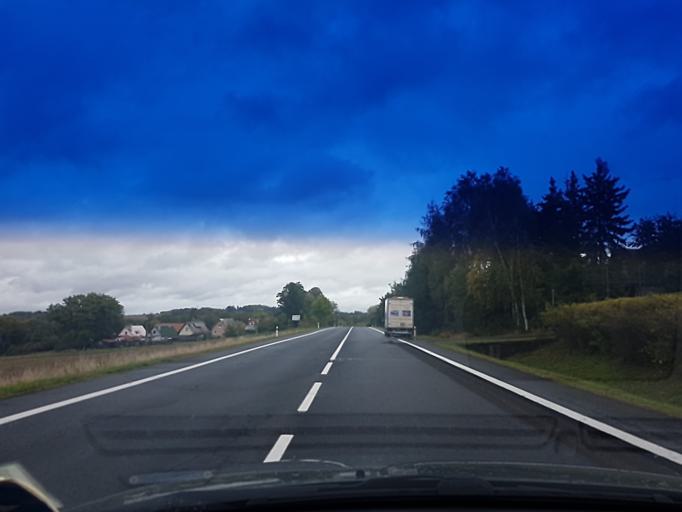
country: CZ
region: Karlovarsky
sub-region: Okres Cheb
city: Frantiskovy Lazne
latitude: 50.0815
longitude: 12.3234
